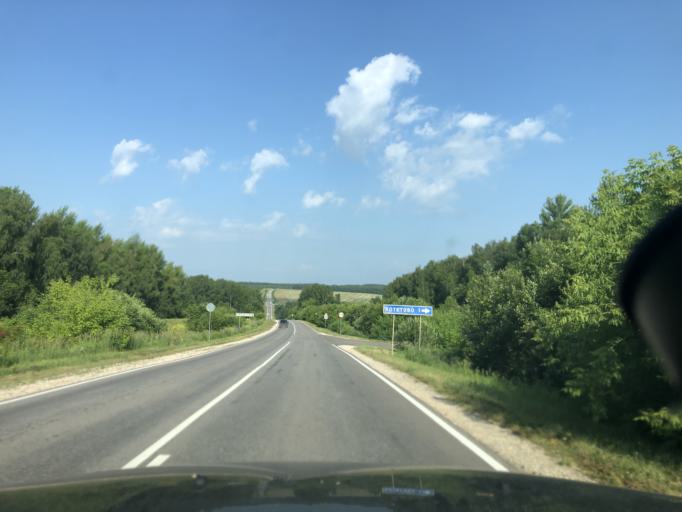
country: RU
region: Tula
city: Dubna
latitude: 54.1279
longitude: 37.0590
